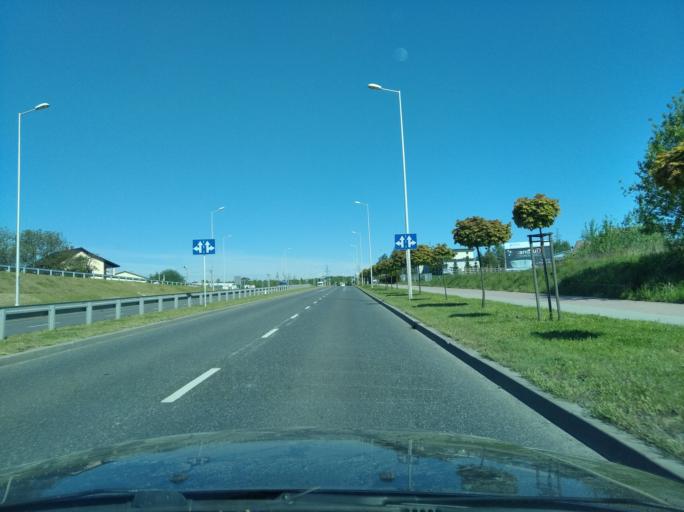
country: PL
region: Subcarpathian Voivodeship
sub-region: Powiat rzeszowski
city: Boguchwala
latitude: 50.0113
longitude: 21.9638
